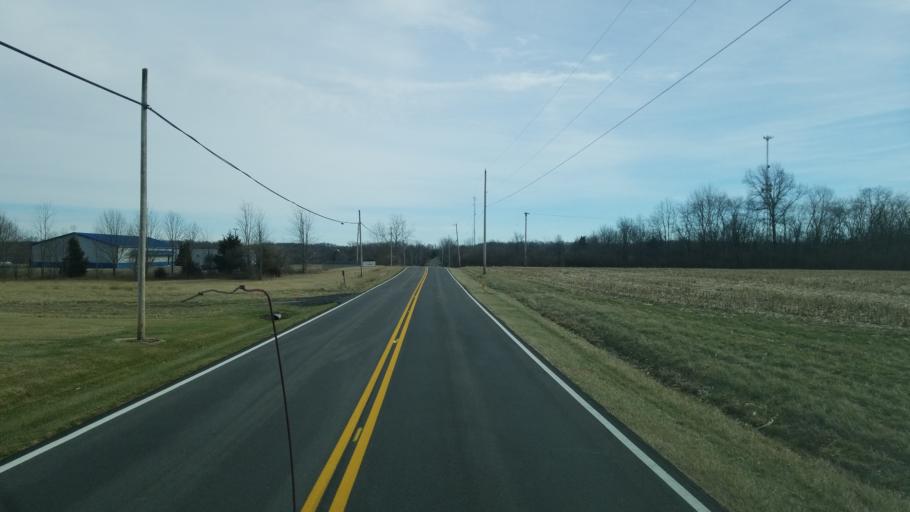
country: US
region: Ohio
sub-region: Warren County
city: Morrow
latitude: 39.4297
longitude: -84.0907
